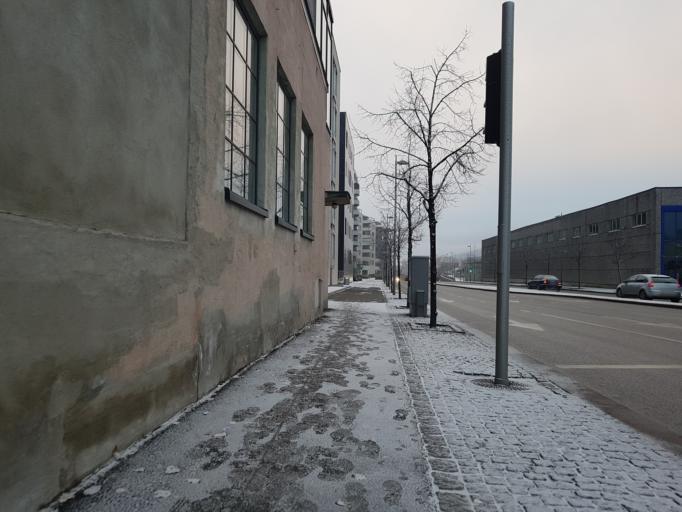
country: NO
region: Buskerud
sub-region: Drammen
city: Drammen
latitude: 59.7432
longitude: 10.1911
